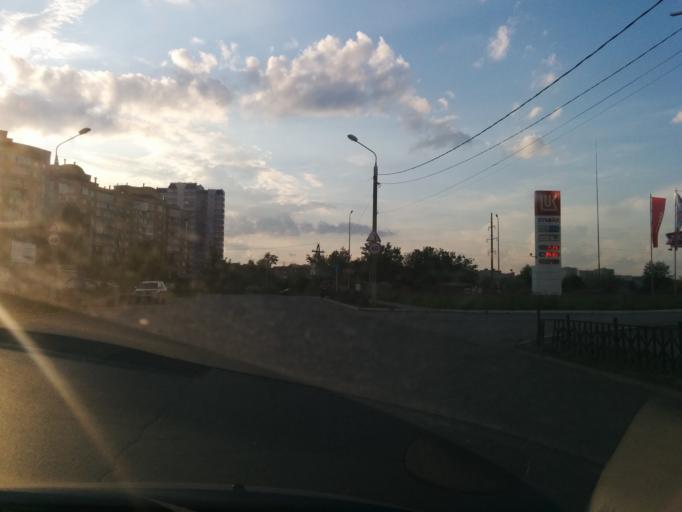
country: RU
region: Perm
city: Perm
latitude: 58.0125
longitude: 56.3060
